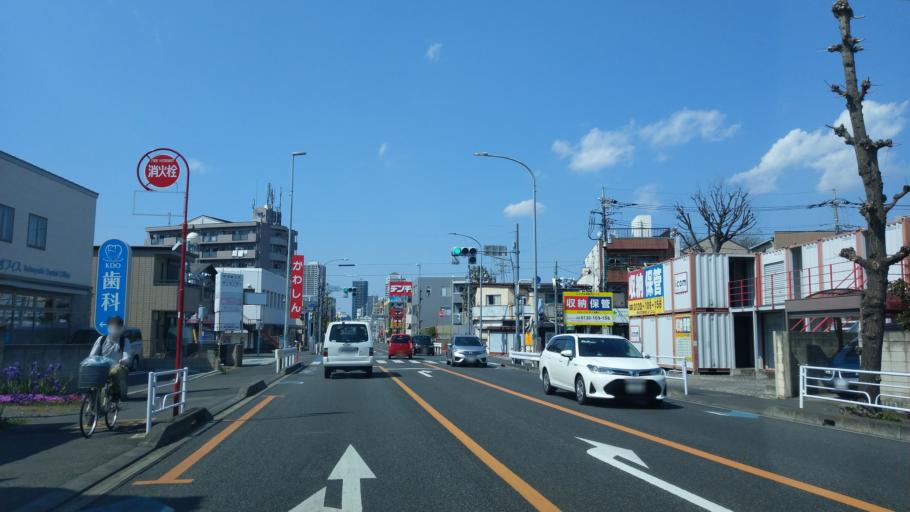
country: JP
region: Saitama
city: Yono
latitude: 35.8801
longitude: 139.6340
